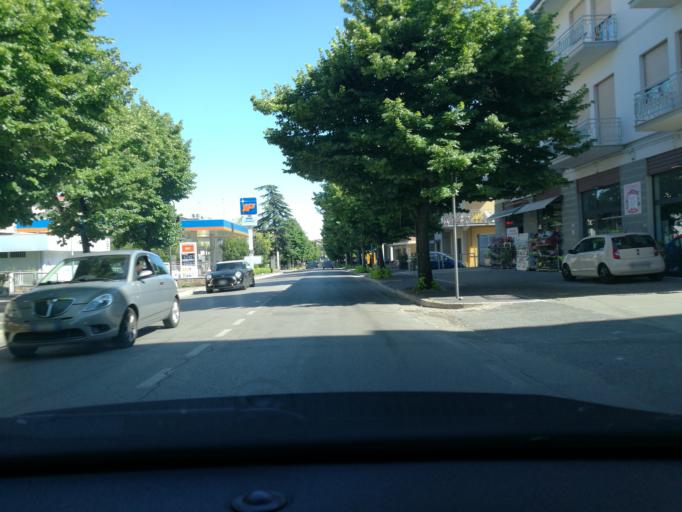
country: IT
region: Abruzzo
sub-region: Provincia di Chieti
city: Vasto
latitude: 42.1226
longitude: 14.7052
